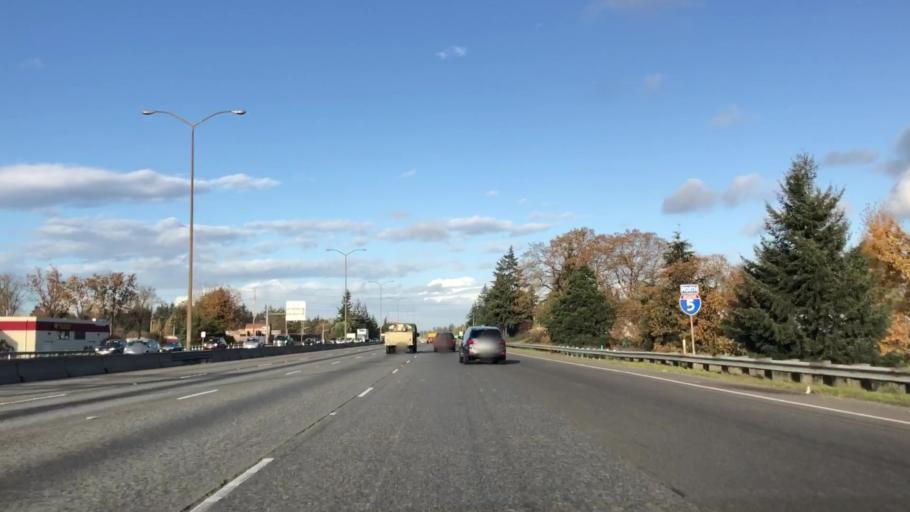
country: US
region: Washington
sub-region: Pierce County
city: McChord Air Force Base
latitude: 47.1677
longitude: -122.4748
